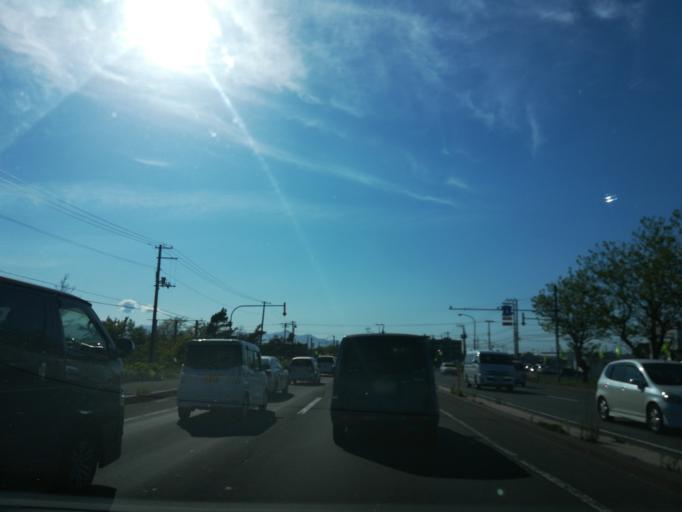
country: JP
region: Hokkaido
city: Kitahiroshima
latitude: 43.0117
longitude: 141.5093
